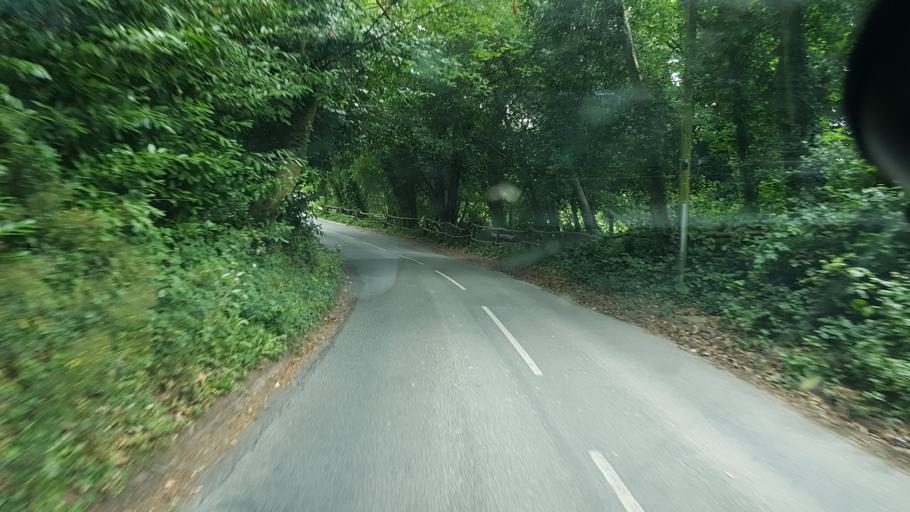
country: GB
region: England
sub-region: West Sussex
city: East Grinstead
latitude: 51.1062
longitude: -0.0246
